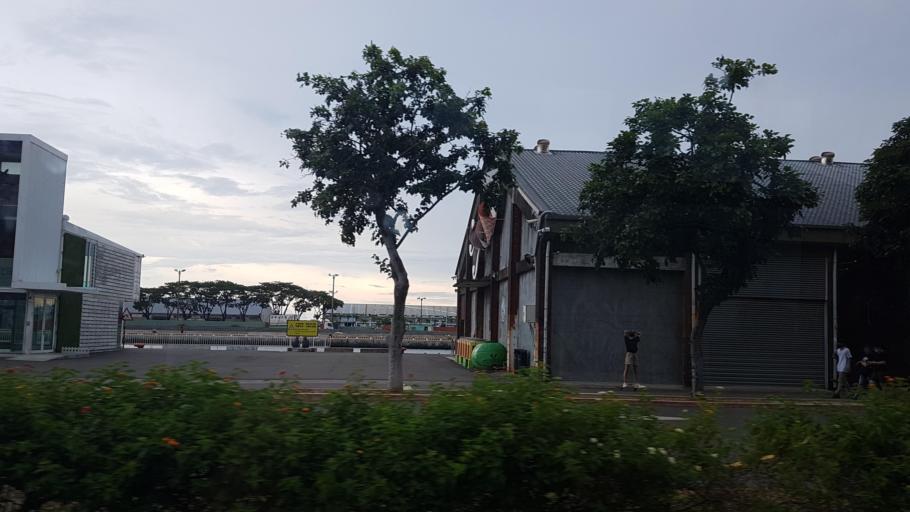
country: TW
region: Kaohsiung
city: Kaohsiung
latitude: 22.6189
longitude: 120.2833
